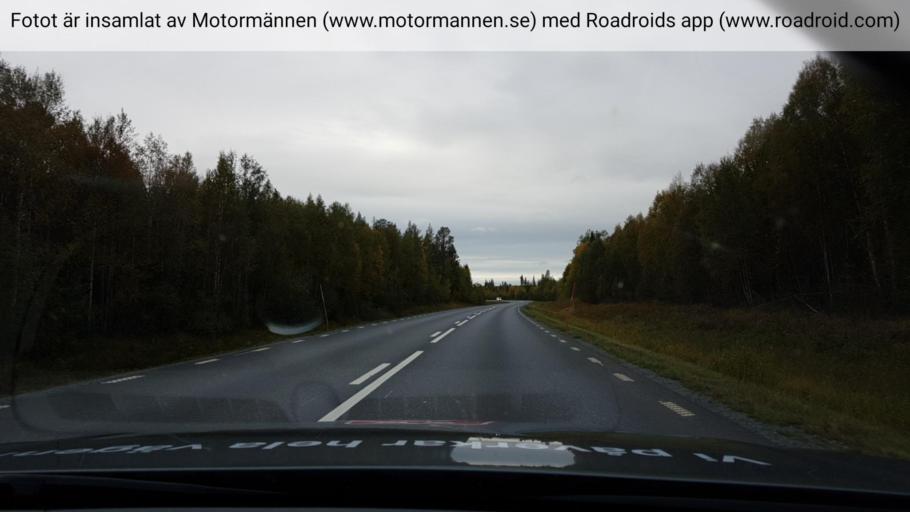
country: SE
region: Vaesterbotten
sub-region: Dorotea Kommun
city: Dorotea
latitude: 64.3446
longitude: 16.6496
